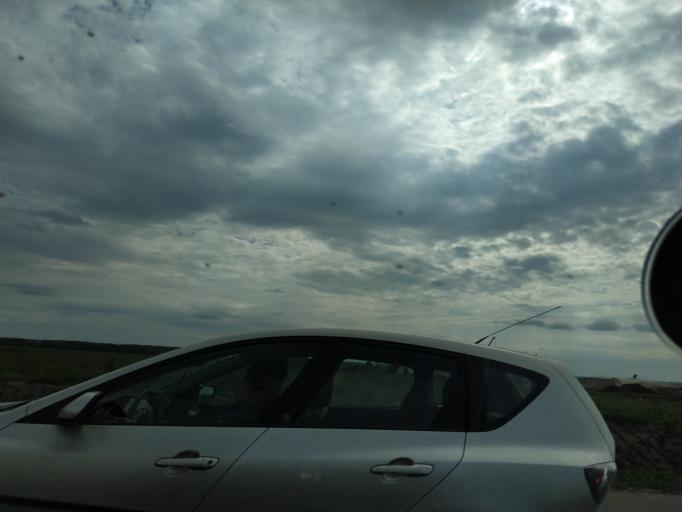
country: RU
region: Moskovskaya
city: Malyshevo
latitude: 55.5060
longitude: 38.2904
